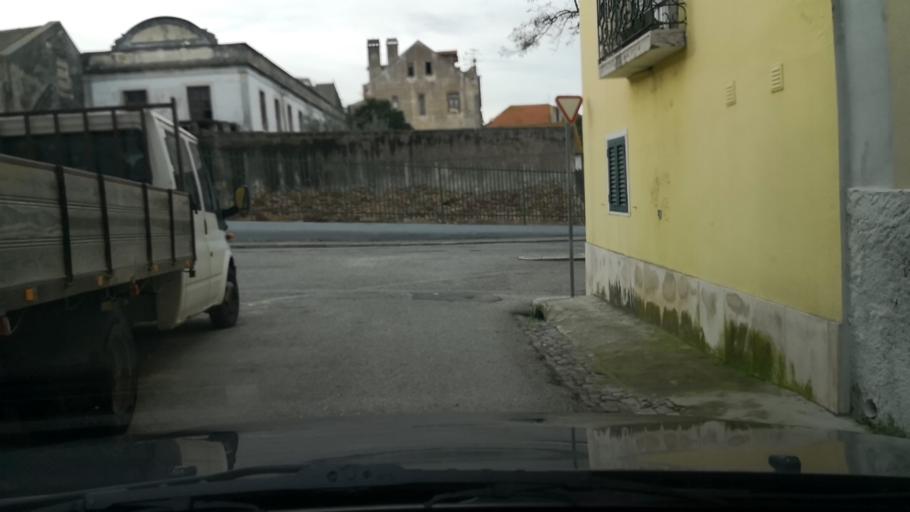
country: PT
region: Setubal
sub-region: Setubal
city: Setubal
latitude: 38.5241
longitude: -8.8860
